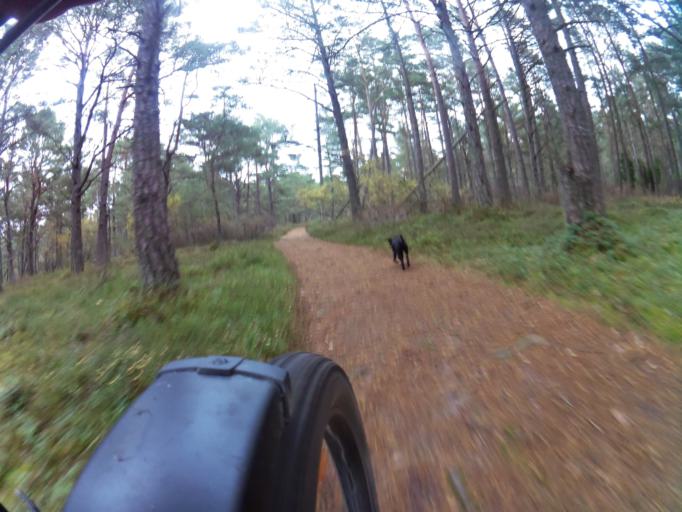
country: PL
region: Pomeranian Voivodeship
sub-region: Powiat leborski
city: Leba
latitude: 54.7761
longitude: 17.6867
